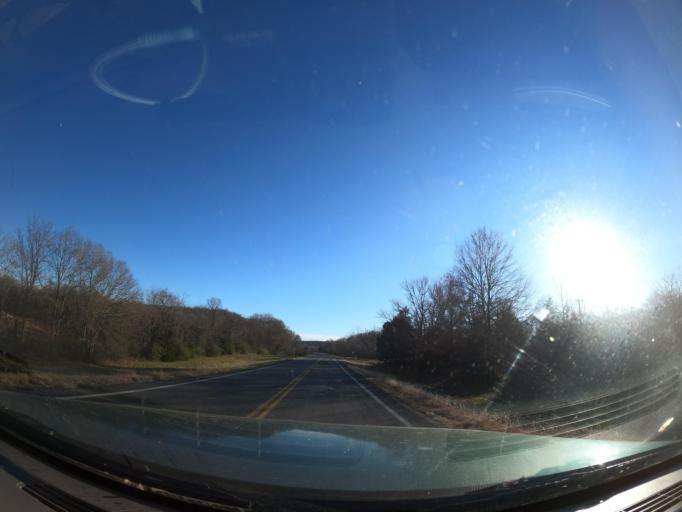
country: US
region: Oklahoma
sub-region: Latimer County
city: Wilburton
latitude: 34.9404
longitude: -95.3412
